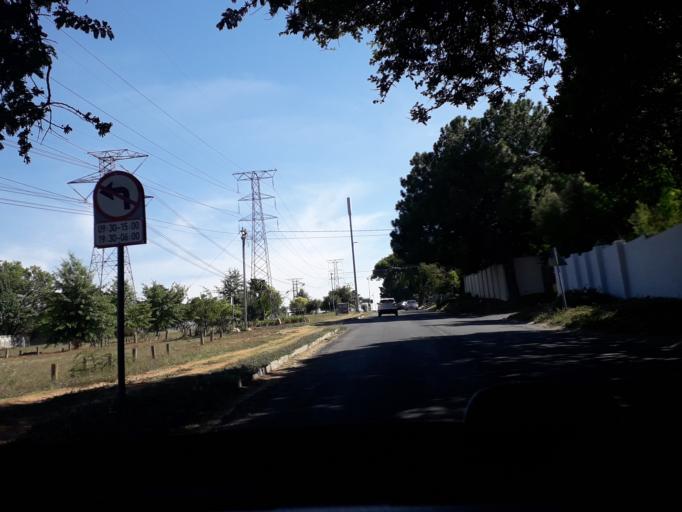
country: ZA
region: Gauteng
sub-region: City of Johannesburg Metropolitan Municipality
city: Johannesburg
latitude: -26.0972
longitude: 28.0392
